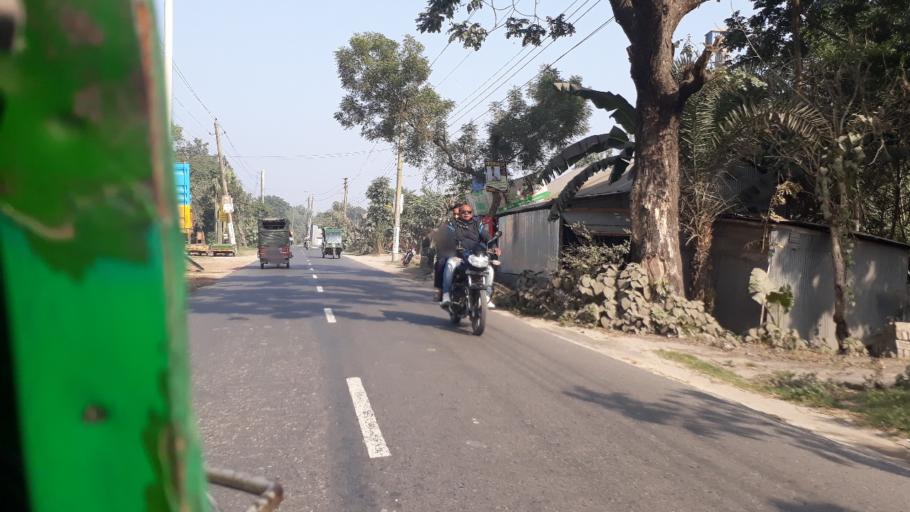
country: BD
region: Khulna
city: Kushtia
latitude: 23.8774
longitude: 89.0847
